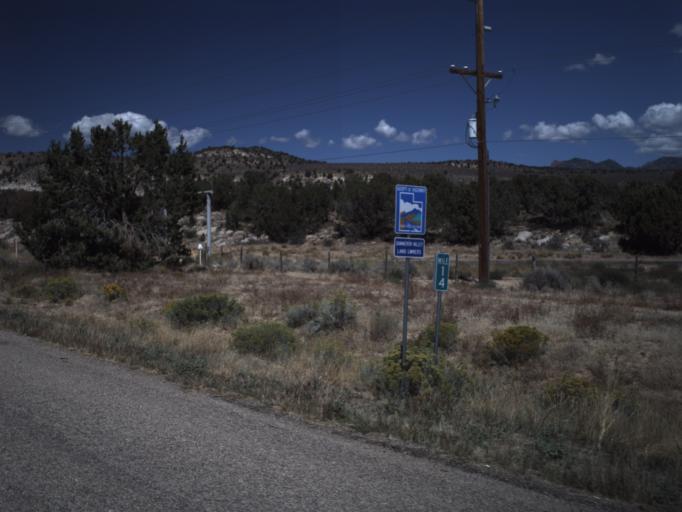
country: US
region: Utah
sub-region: Washington County
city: Ivins
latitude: 37.2654
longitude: -113.6372
